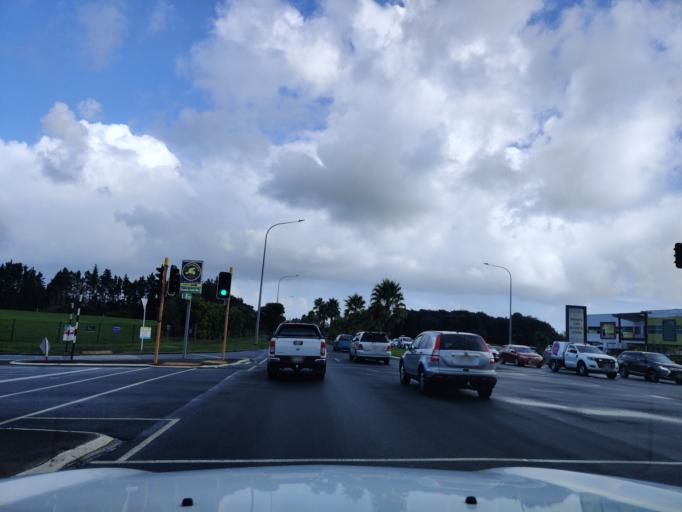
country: NZ
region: Auckland
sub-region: Auckland
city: Manukau City
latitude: -36.9592
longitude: 174.9035
